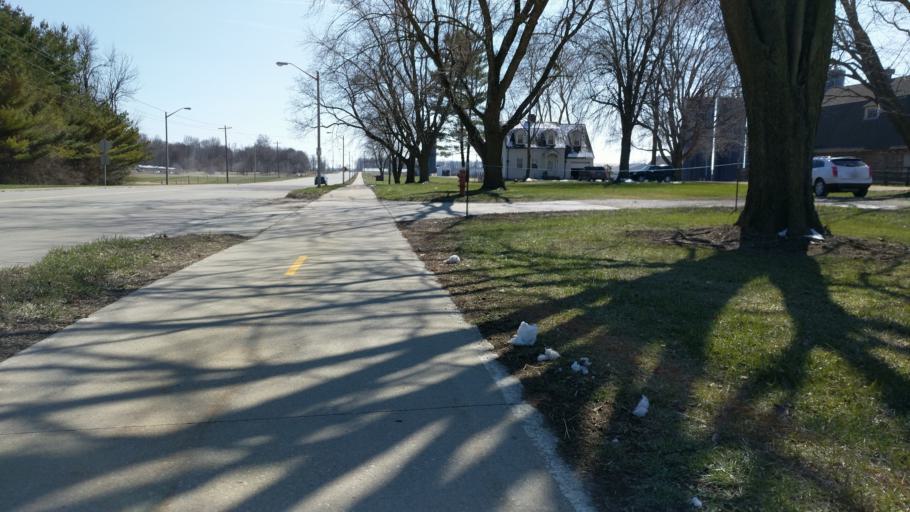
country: US
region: Illinois
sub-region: Champaign County
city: Urbana
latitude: 40.0897
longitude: -88.2191
